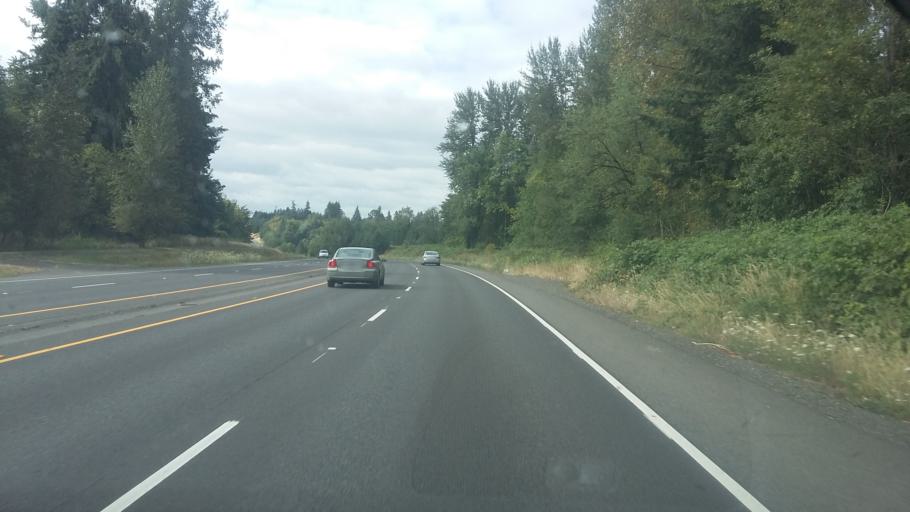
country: US
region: Washington
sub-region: Clark County
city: Brush Prairie
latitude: 45.7467
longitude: -122.5512
